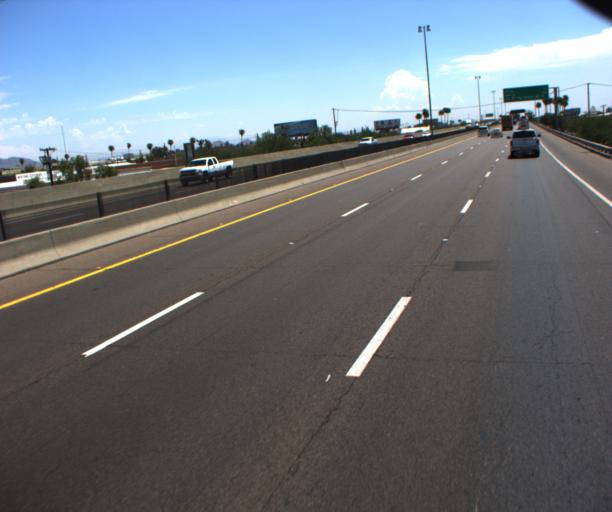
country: US
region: Arizona
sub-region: Maricopa County
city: Phoenix
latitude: 33.4287
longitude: -112.0771
